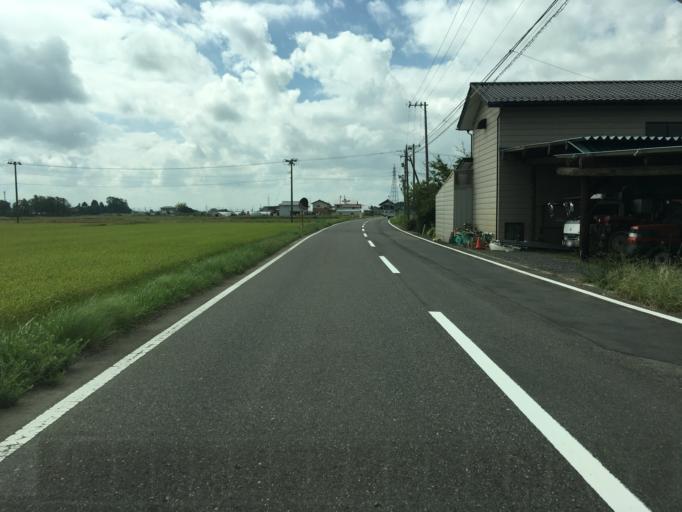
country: JP
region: Fukushima
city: Motomiya
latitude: 37.4696
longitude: 140.3406
